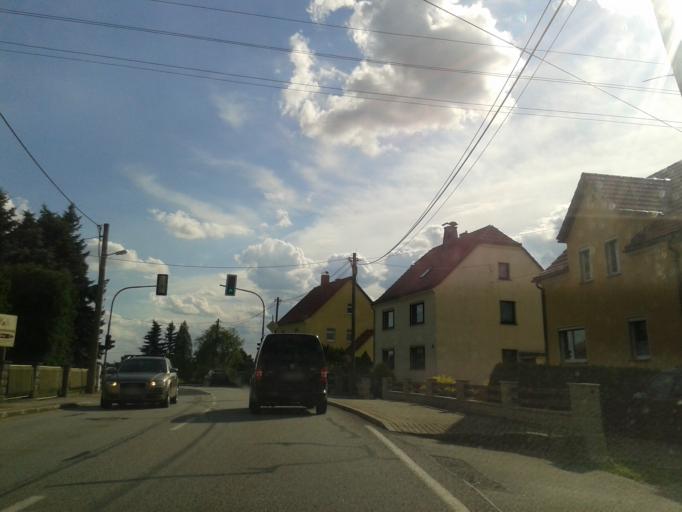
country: DE
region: Saxony
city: Lichtenberg
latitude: 51.1516
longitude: 13.9631
